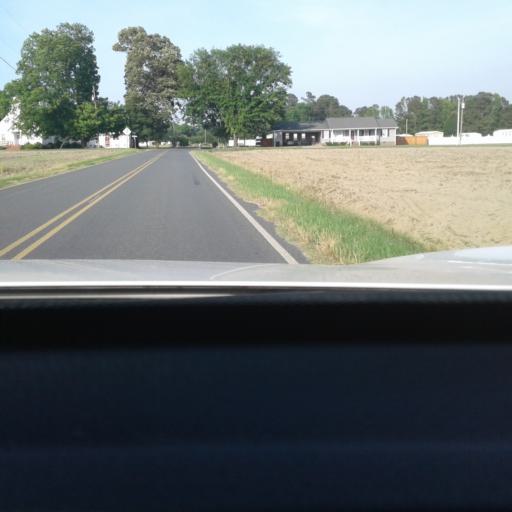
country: US
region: North Carolina
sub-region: Harnett County
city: Dunn
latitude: 35.3430
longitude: -78.5794
